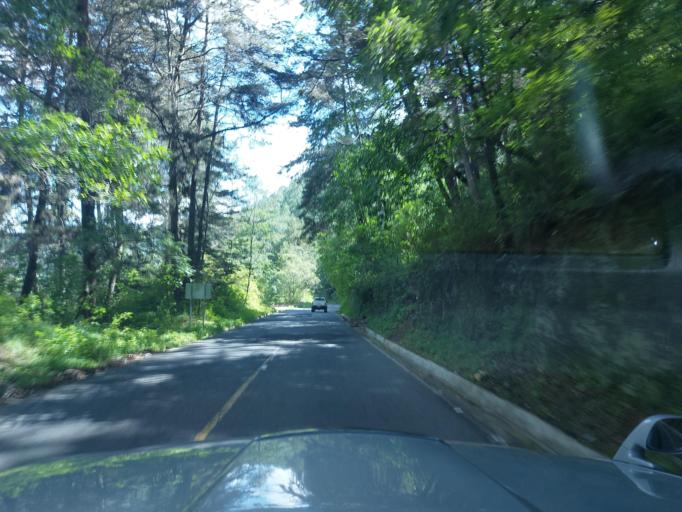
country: GT
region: Chimaltenango
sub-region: Municipio de Santa Cruz Balanya
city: Santa Cruz Balanya
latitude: 14.6862
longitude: -90.8961
